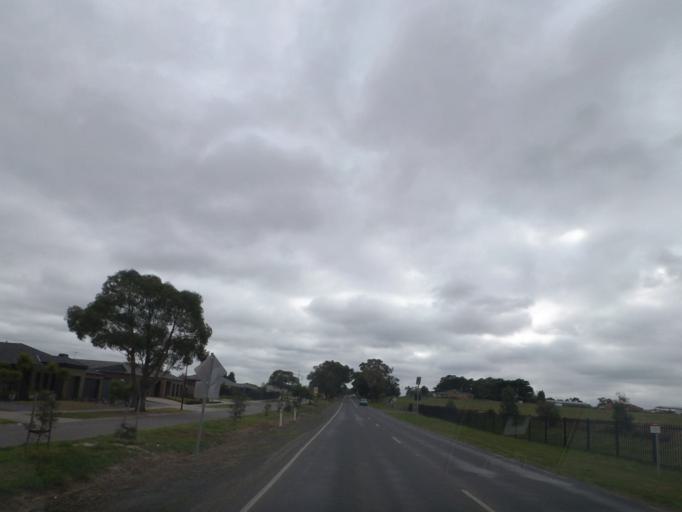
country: AU
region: Victoria
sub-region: Nillumbik
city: Doreen
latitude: -37.6118
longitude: 145.1371
